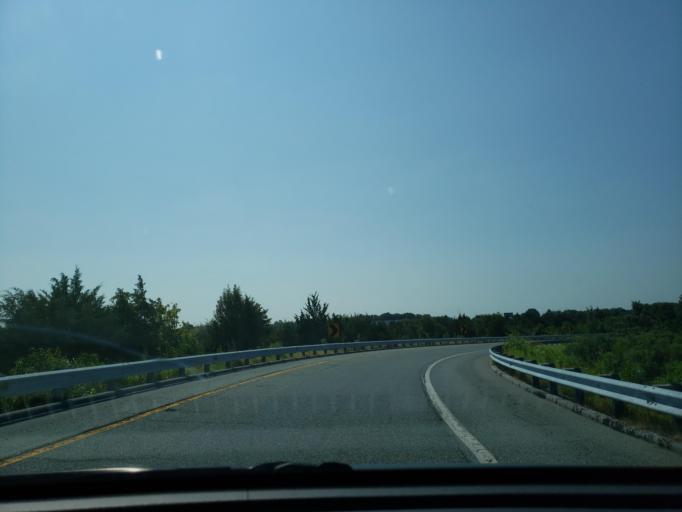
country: US
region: Delaware
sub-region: Kent County
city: Dover
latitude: 39.1464
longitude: -75.4980
